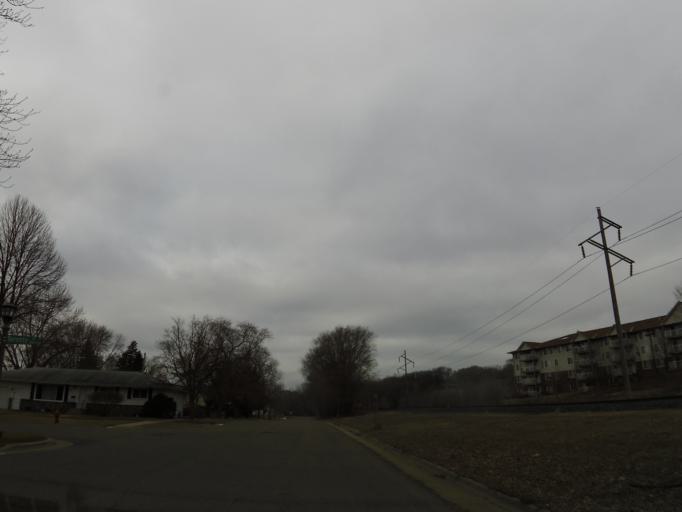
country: US
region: Minnesota
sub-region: Dakota County
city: West Saint Paul
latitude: 44.9324
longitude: -93.1253
